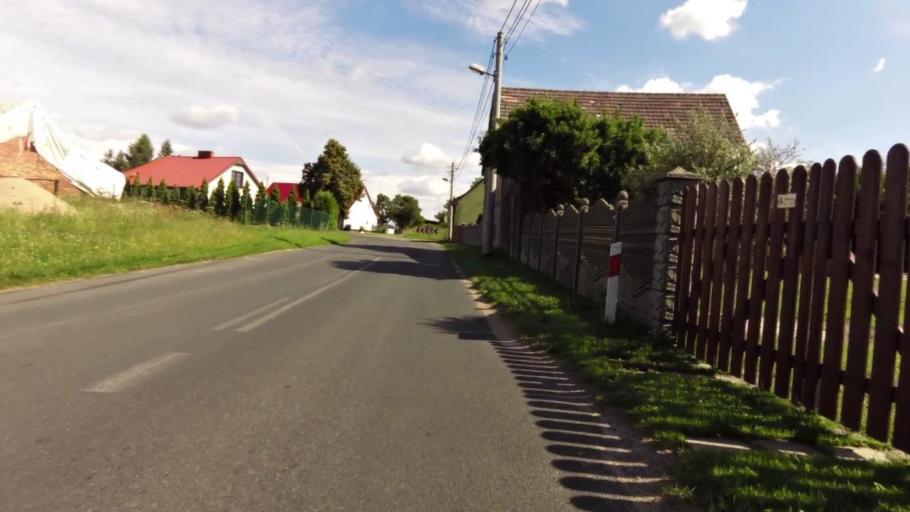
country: PL
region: West Pomeranian Voivodeship
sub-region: Powiat stargardzki
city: Dobrzany
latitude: 53.4042
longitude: 15.4327
